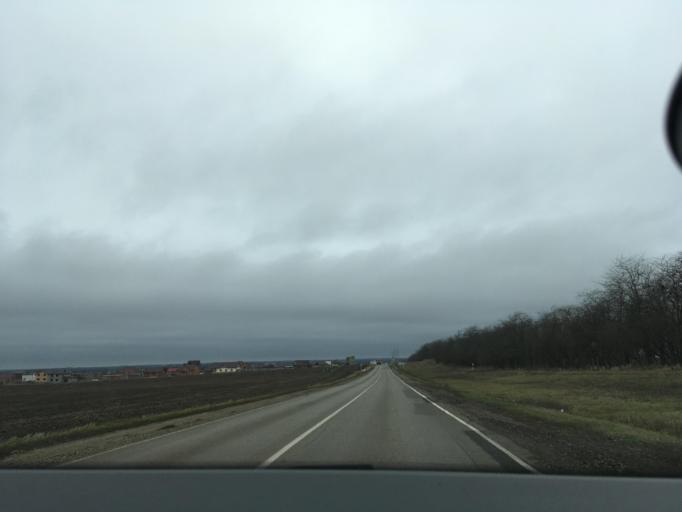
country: RU
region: Krasnodarskiy
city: Kushchevskaya
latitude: 46.5892
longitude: 39.6440
